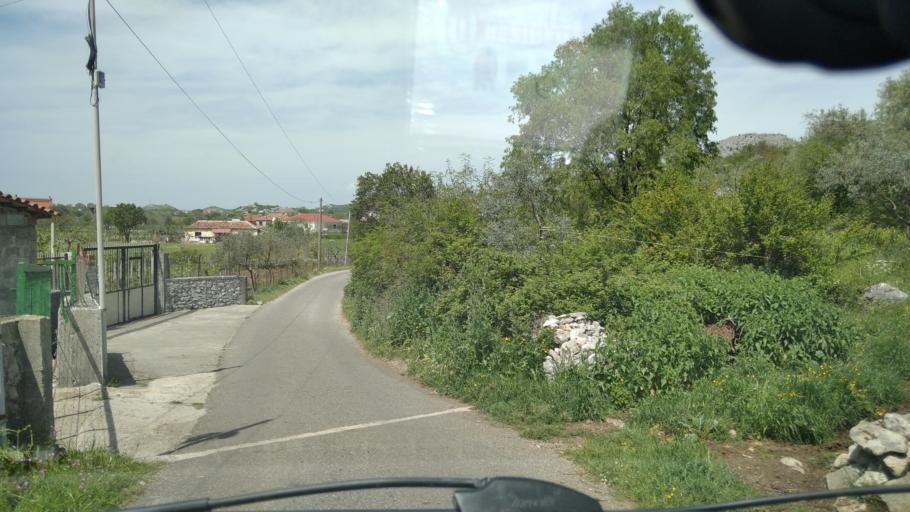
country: AL
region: Shkoder
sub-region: Rrethi i Malesia e Madhe
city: Gruemire
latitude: 42.1439
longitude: 19.5462
